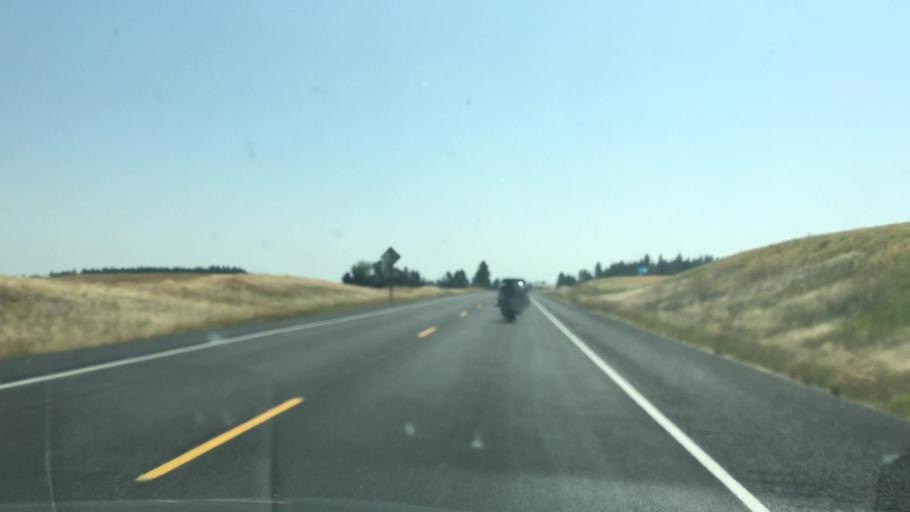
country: US
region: Idaho
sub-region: Nez Perce County
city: Lapwai
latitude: 46.2433
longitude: -116.5870
